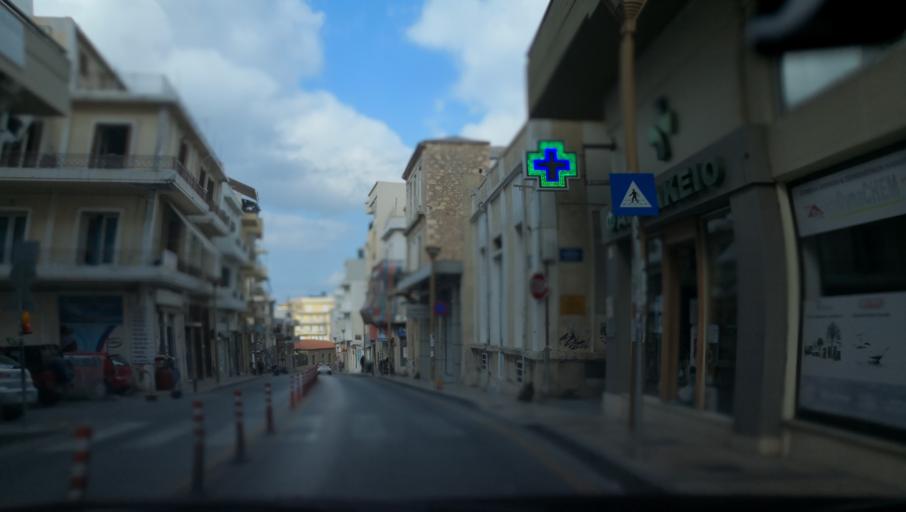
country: GR
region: Crete
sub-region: Nomos Irakleiou
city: Irakleion
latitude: 35.3388
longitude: 25.1297
